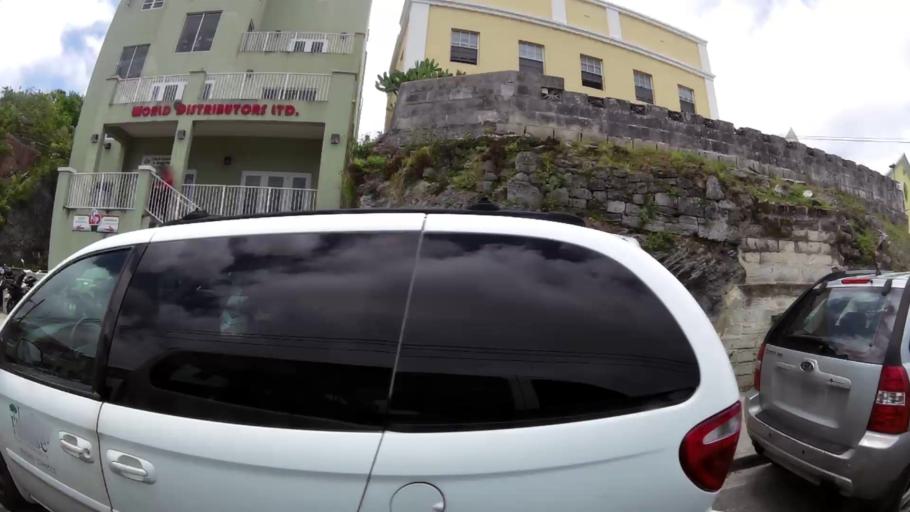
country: BM
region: Hamilton city
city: Hamilton
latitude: 32.2991
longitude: -64.7826
